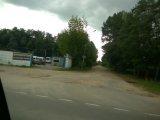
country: RU
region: Moskovskaya
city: Bykovo
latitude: 55.6190
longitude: 38.0931
